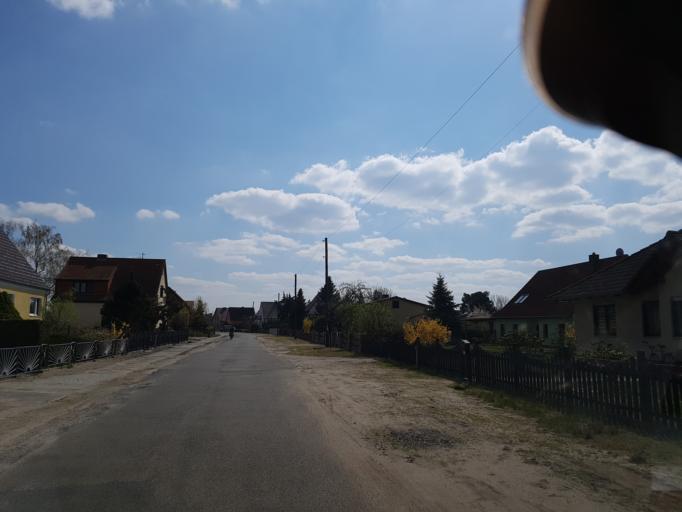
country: DE
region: Brandenburg
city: Bruck
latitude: 52.1928
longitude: 12.7545
